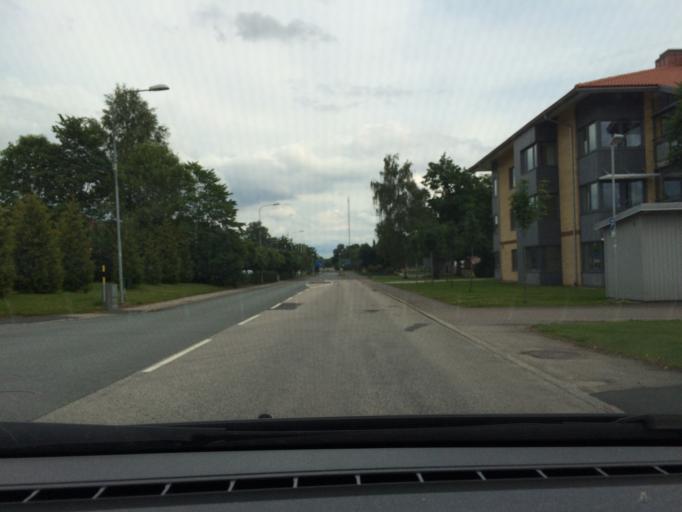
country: SE
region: Joenkoeping
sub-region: Varnamo Kommun
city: Forsheda
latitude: 57.1644
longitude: 13.8315
